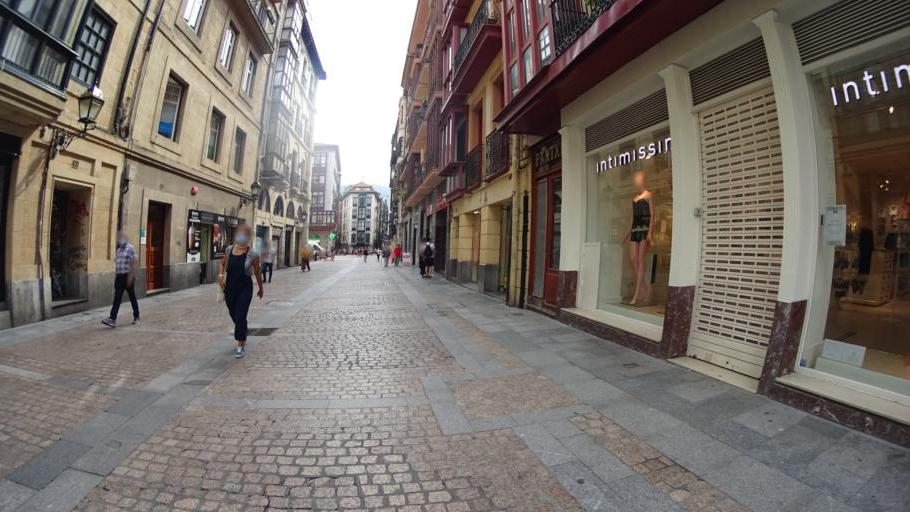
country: ES
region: Basque Country
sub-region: Bizkaia
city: Bilbao
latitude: 43.2582
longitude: -2.9221
